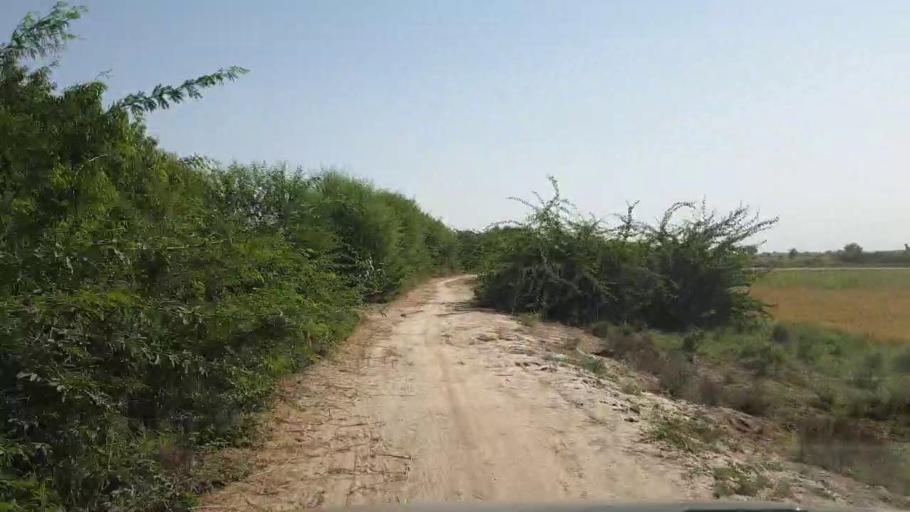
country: PK
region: Sindh
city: Kadhan
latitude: 24.6042
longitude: 69.0033
